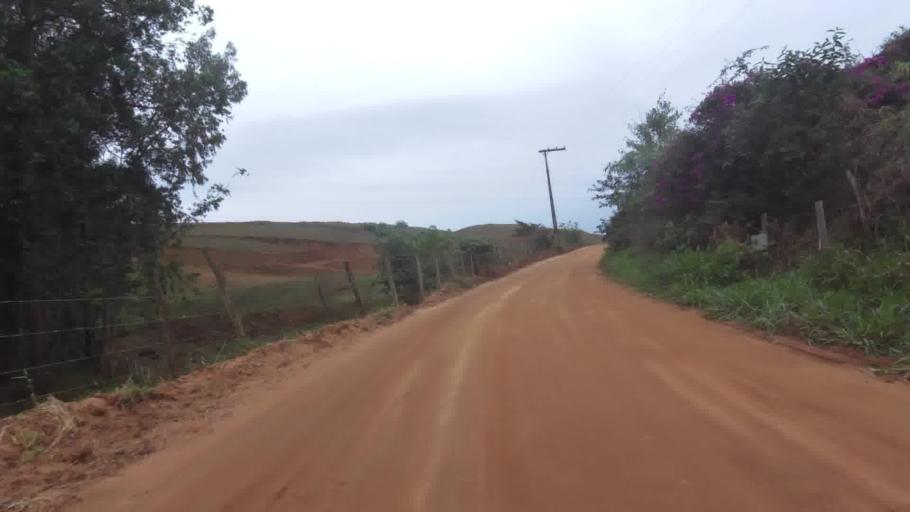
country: BR
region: Espirito Santo
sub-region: Iconha
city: Iconha
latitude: -20.7994
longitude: -40.8178
